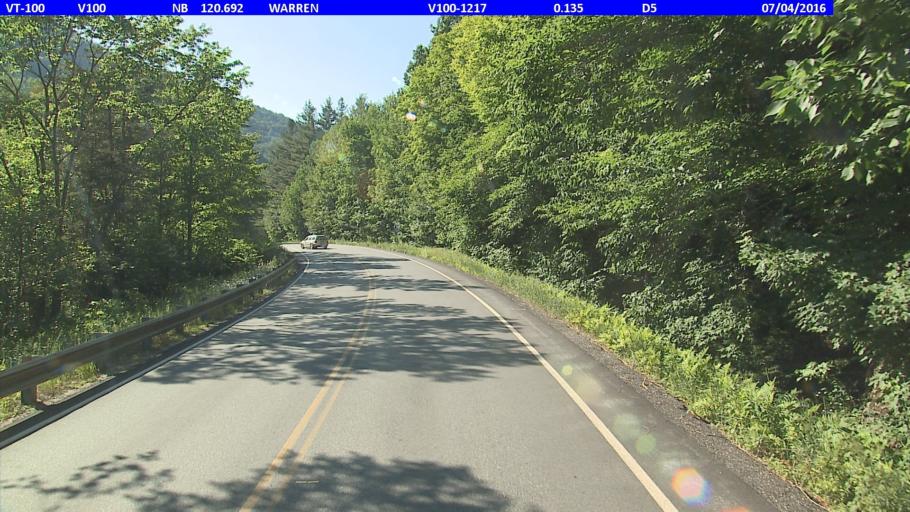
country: US
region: Vermont
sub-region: Washington County
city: Northfield
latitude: 44.0630
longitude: -72.8533
